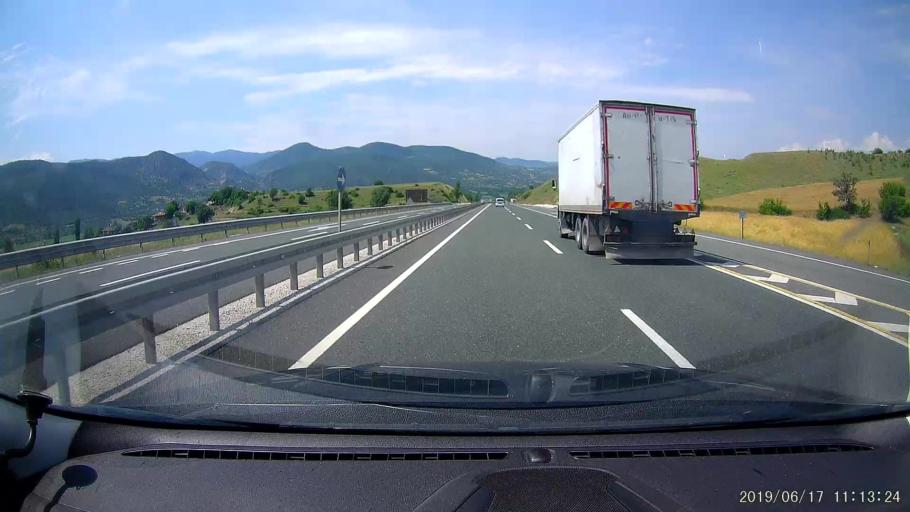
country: TR
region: Kastamonu
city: Tosya
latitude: 40.9628
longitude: 33.9731
